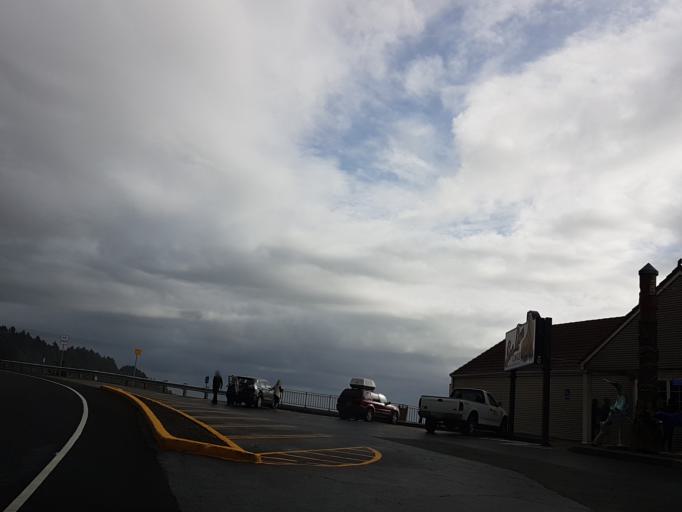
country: US
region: Oregon
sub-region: Lane County
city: Florence
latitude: 44.1220
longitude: -124.1265
